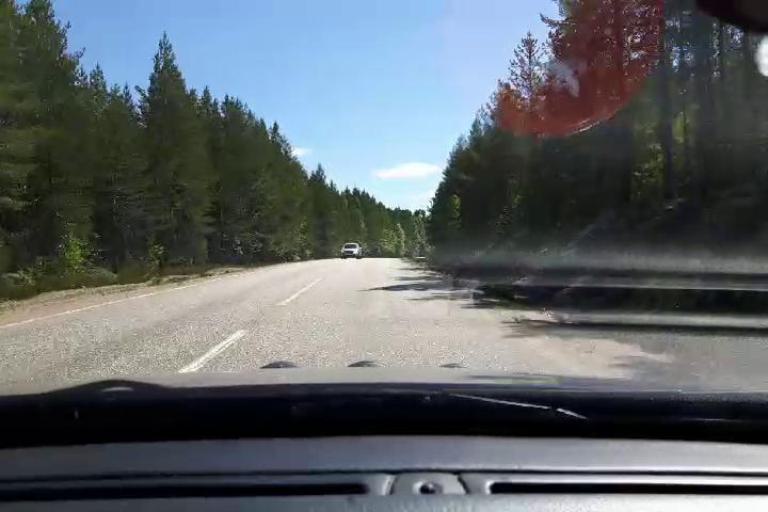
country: SE
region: Vaesternorrland
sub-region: Ange Kommun
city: Ange
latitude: 62.0910
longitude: 15.0907
